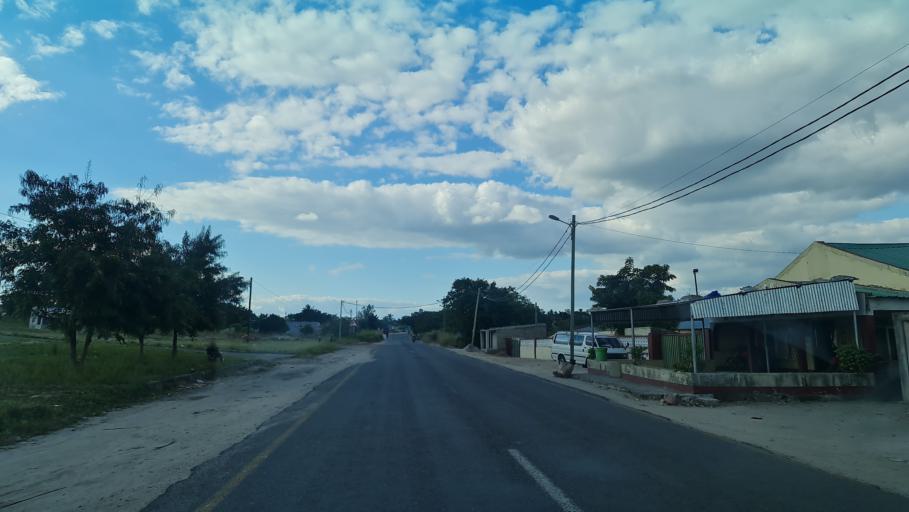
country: MZ
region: Manica
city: Chimoio
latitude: -19.2151
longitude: 33.9233
